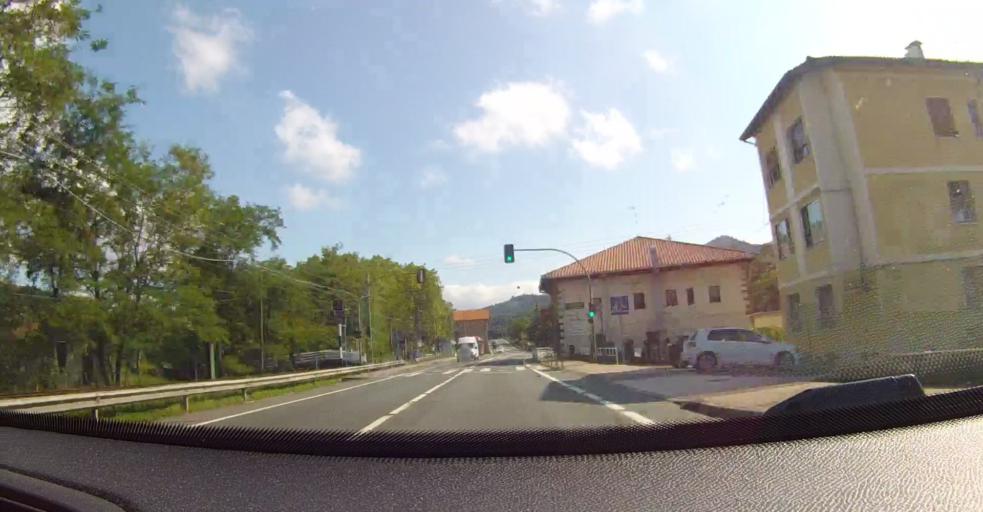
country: ES
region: Basque Country
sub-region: Bizkaia
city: Muxika
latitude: 43.2880
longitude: -2.6894
